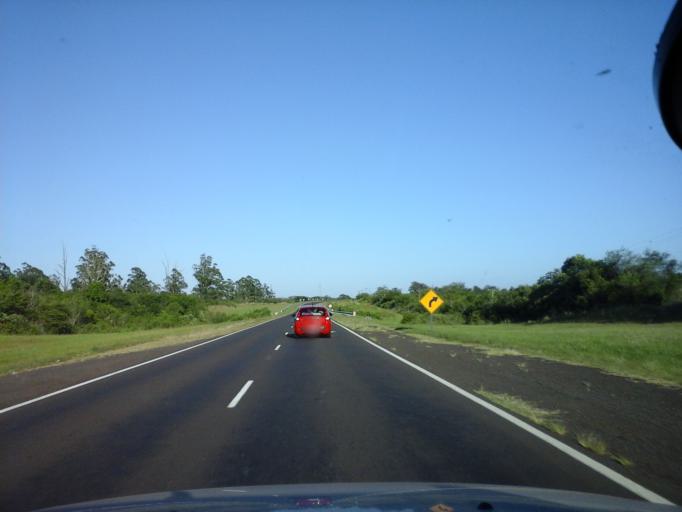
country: AR
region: Corrientes
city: Ita Ibate
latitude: -27.4871
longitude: -57.2830
